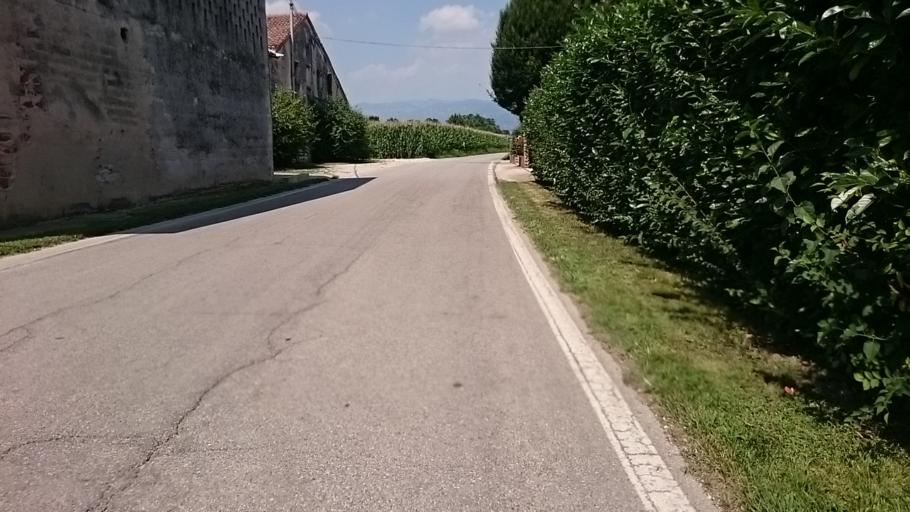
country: IT
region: Veneto
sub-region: Provincia di Vicenza
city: Rosa
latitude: 45.7035
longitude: 11.7415
